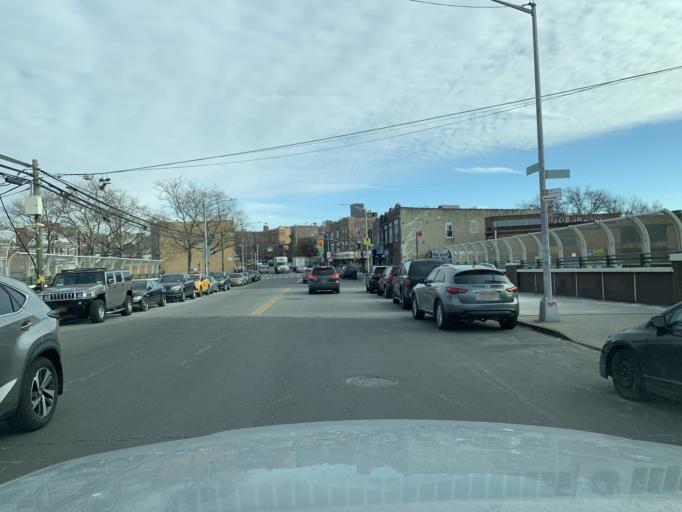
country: US
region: New York
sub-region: Queens County
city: Long Island City
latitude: 40.7429
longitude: -73.8968
